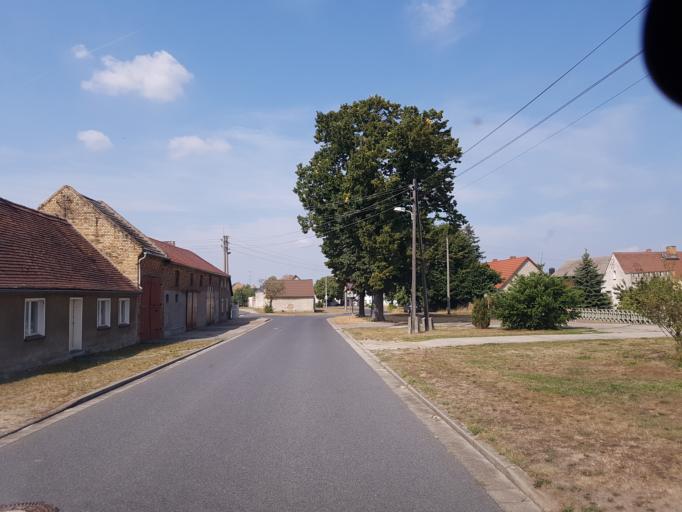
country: DE
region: Brandenburg
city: Finsterwalde
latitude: 51.6649
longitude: 13.7389
